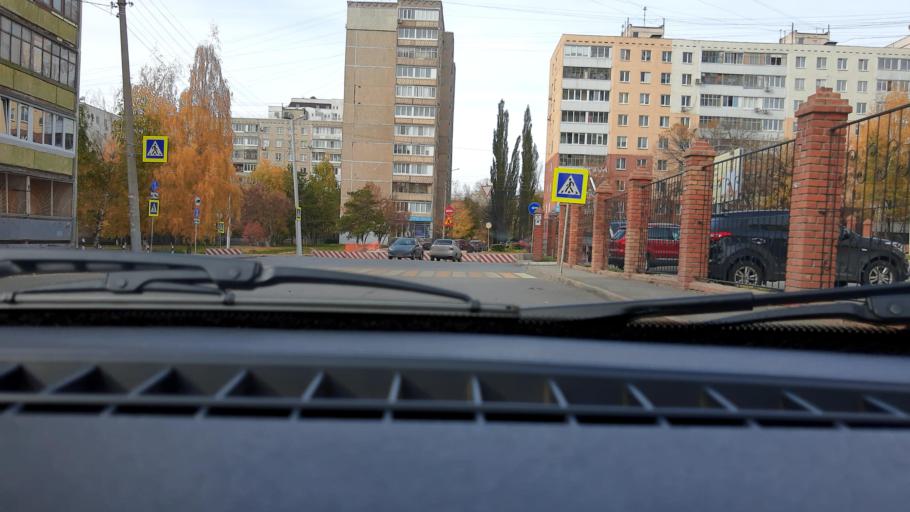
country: RU
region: Bashkortostan
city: Ufa
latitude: 54.7613
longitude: 56.0217
